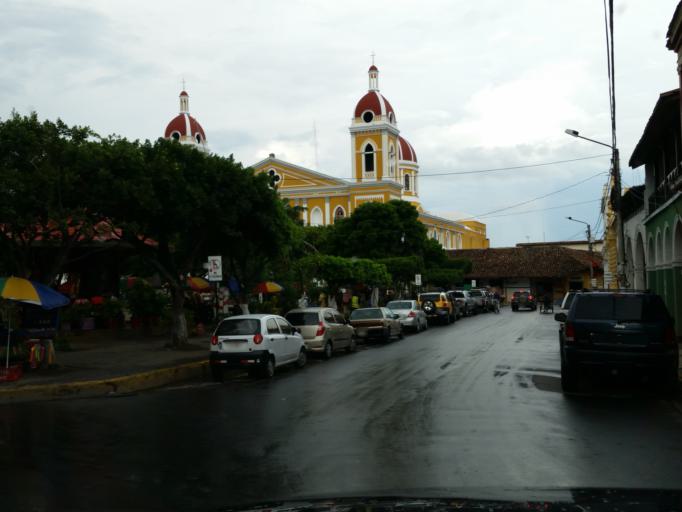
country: NI
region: Granada
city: Granada
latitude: 11.9294
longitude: -85.9544
